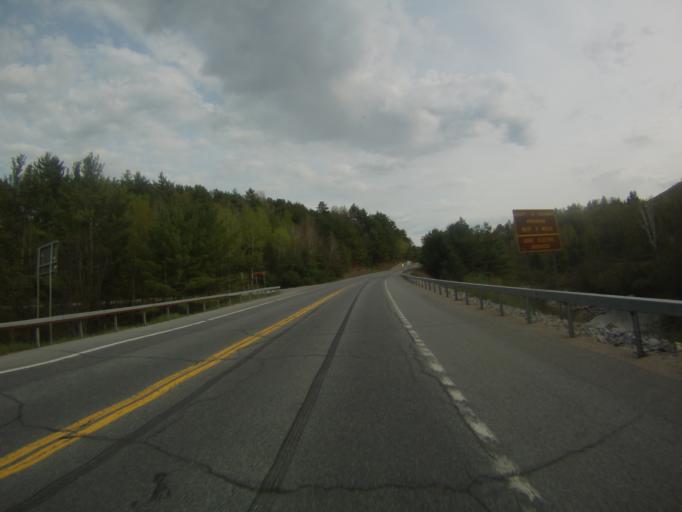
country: US
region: New York
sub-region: Warren County
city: Warrensburg
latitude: 43.6943
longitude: -73.9874
